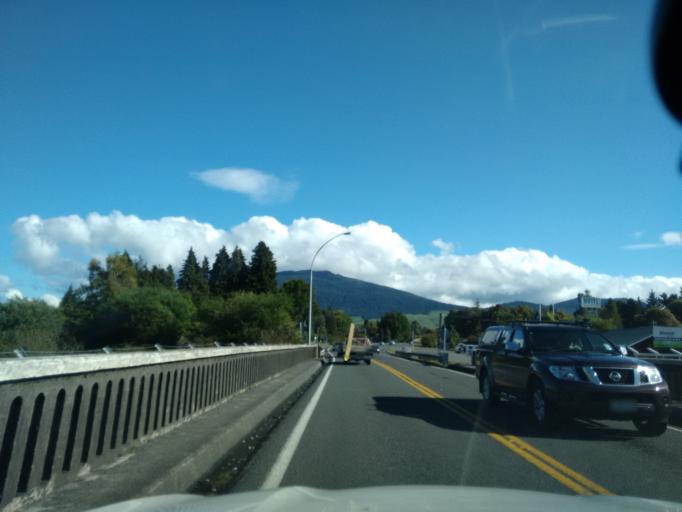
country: NZ
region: Waikato
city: Turangi
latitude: -38.9861
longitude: 175.8188
